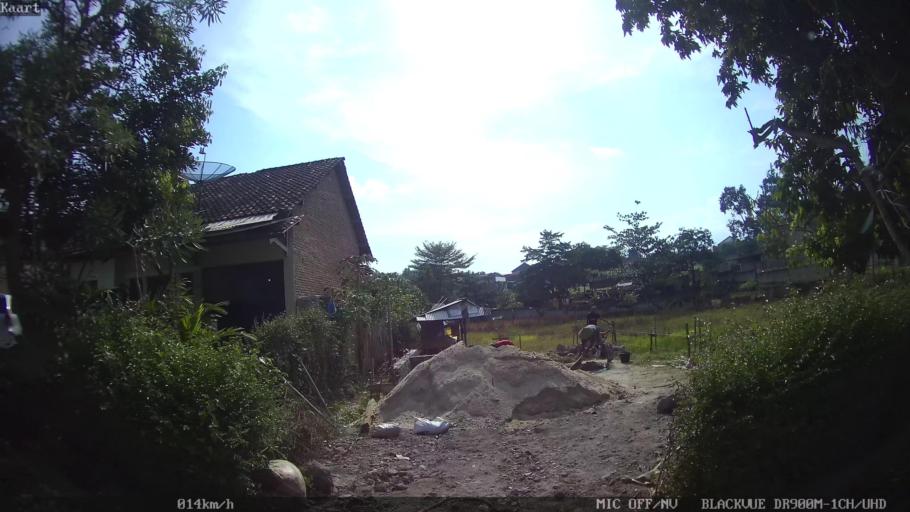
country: ID
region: Lampung
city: Kedaton
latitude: -5.3831
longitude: 105.2305
